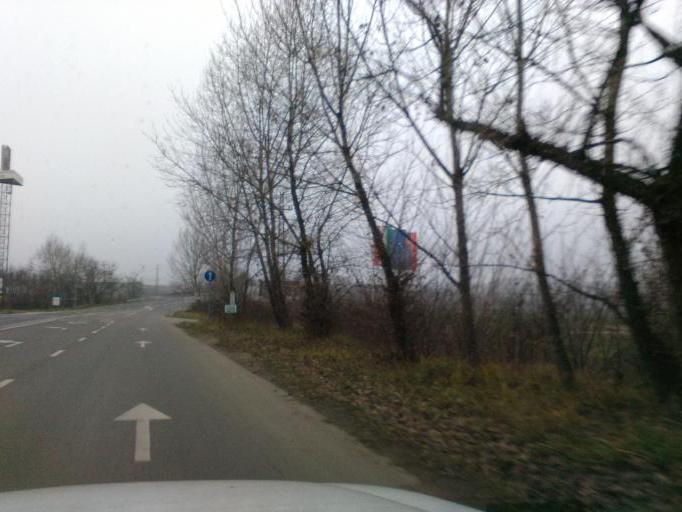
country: HU
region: Pest
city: Toeroekbalint
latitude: 47.4468
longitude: 18.8943
